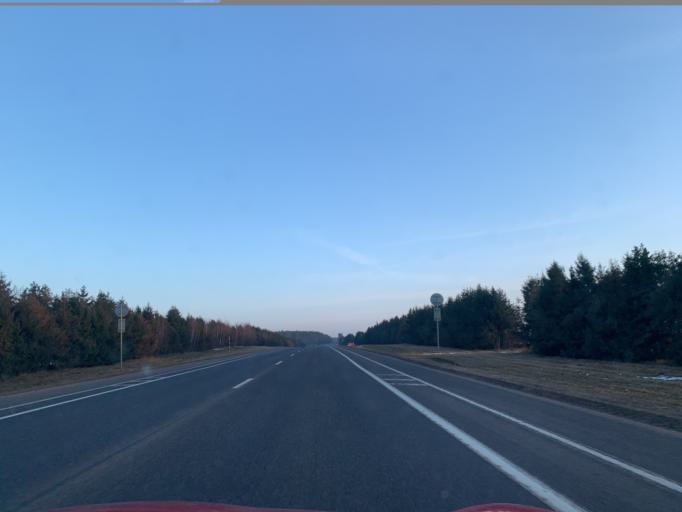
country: BY
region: Minsk
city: Haradzyeya
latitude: 53.2907
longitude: 26.5786
